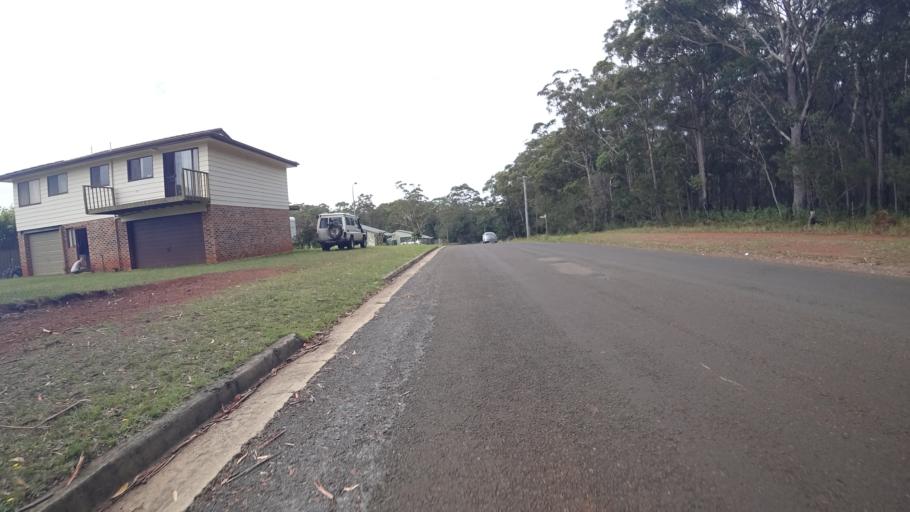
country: AU
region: New South Wales
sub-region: Shoalhaven Shire
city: Milton
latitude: -35.2585
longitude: 150.5052
